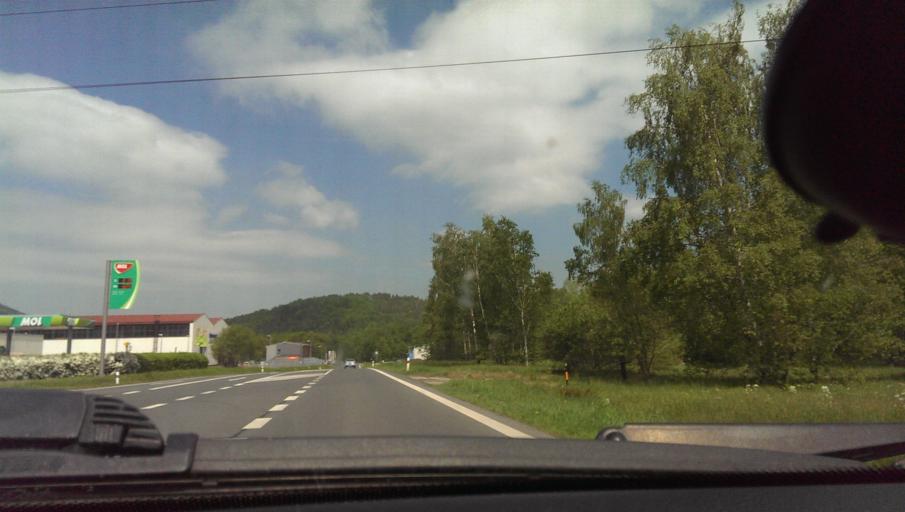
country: CZ
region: Moravskoslezsky
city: Frenstat pod Radhostem
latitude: 49.5551
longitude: 18.1989
